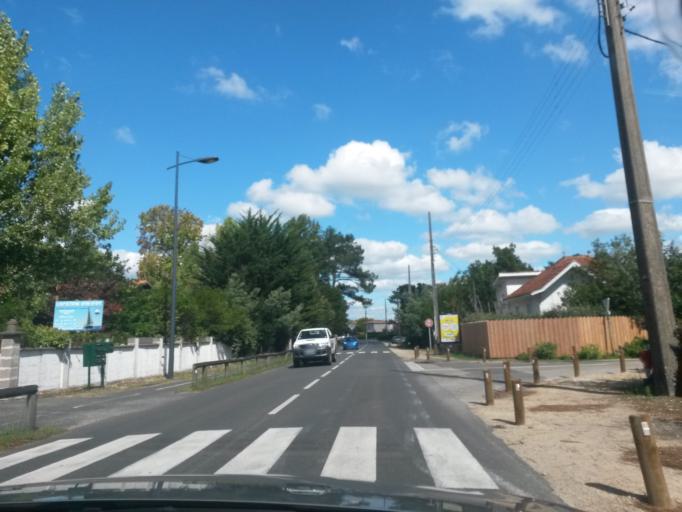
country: FR
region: Aquitaine
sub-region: Departement de la Gironde
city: Ares
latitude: 44.7414
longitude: -1.1856
